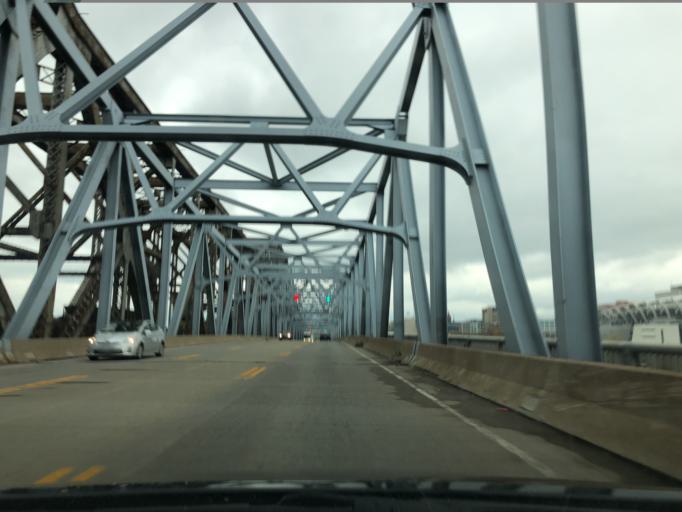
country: US
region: Kentucky
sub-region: Kenton County
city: Covington
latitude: 39.0904
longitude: -84.5191
